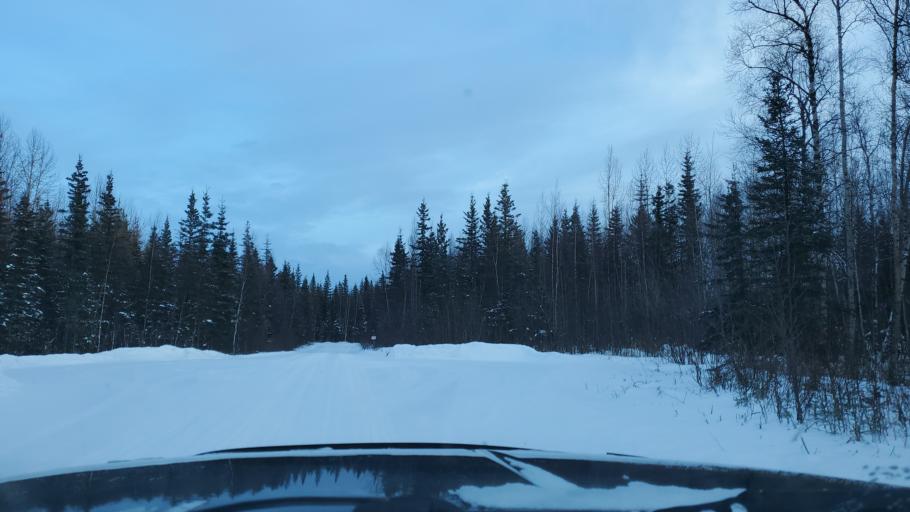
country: US
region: Alaska
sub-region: Matanuska-Susitna Borough
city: Lakes
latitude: 61.6687
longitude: -149.2924
